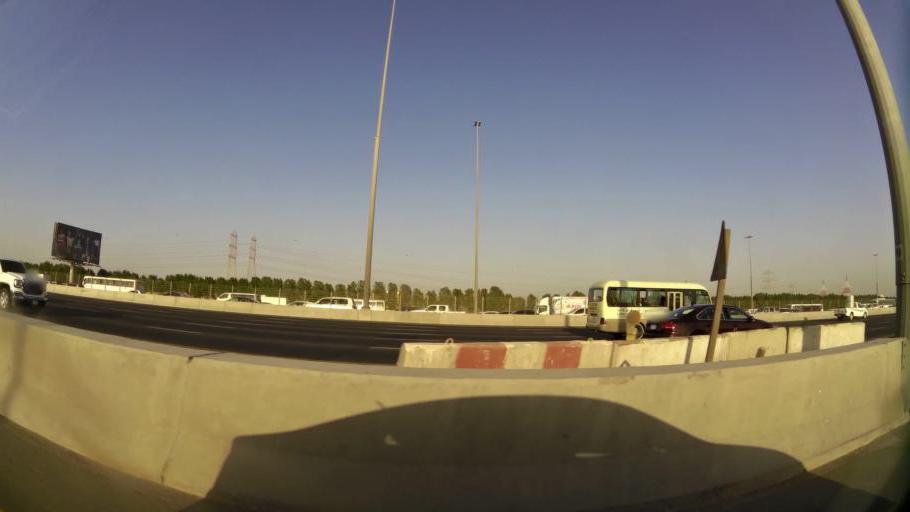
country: AE
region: Ash Shariqah
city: Sharjah
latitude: 25.2396
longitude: 55.4038
